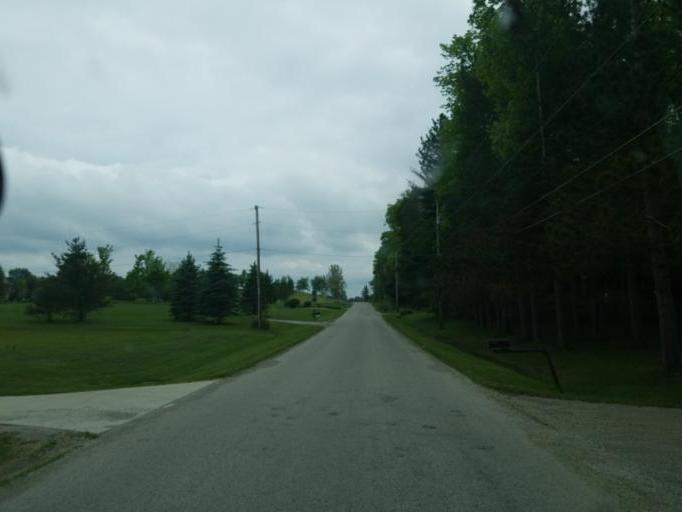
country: US
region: Ohio
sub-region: Richland County
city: Lexington
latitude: 40.6553
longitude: -82.6231
